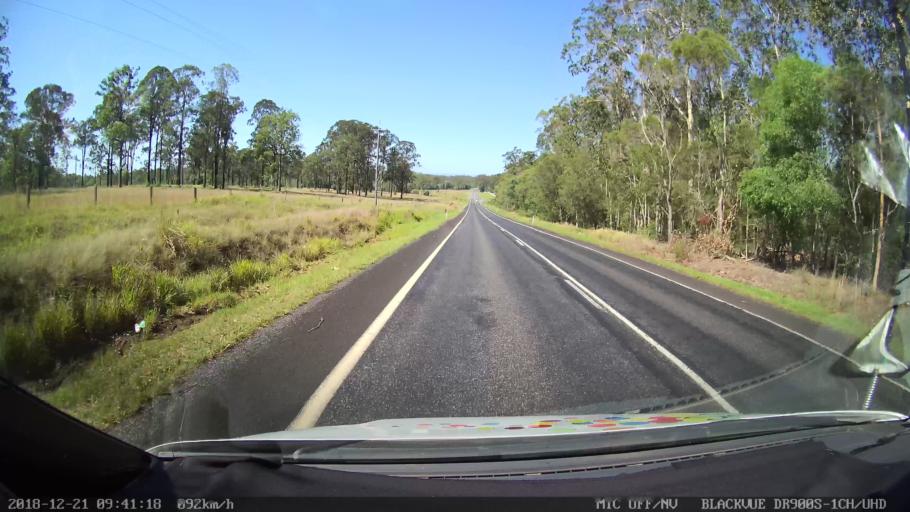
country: AU
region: New South Wales
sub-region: Clarence Valley
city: Grafton
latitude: -29.5835
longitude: 152.9586
